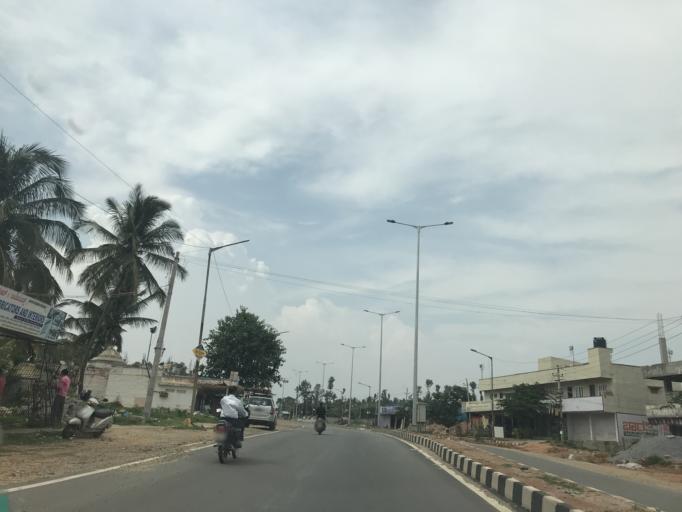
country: IN
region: Karnataka
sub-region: Bangalore Urban
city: Yelahanka
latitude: 13.1022
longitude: 77.6586
